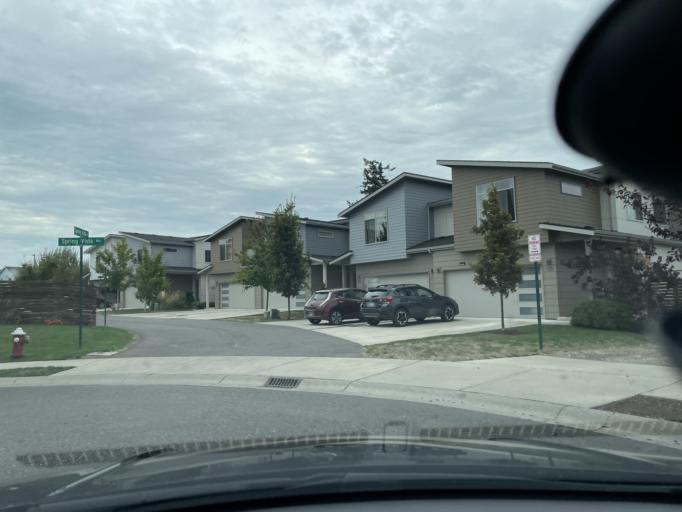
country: US
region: Washington
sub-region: Whatcom County
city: Bellingham
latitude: 48.8138
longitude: -122.4994
